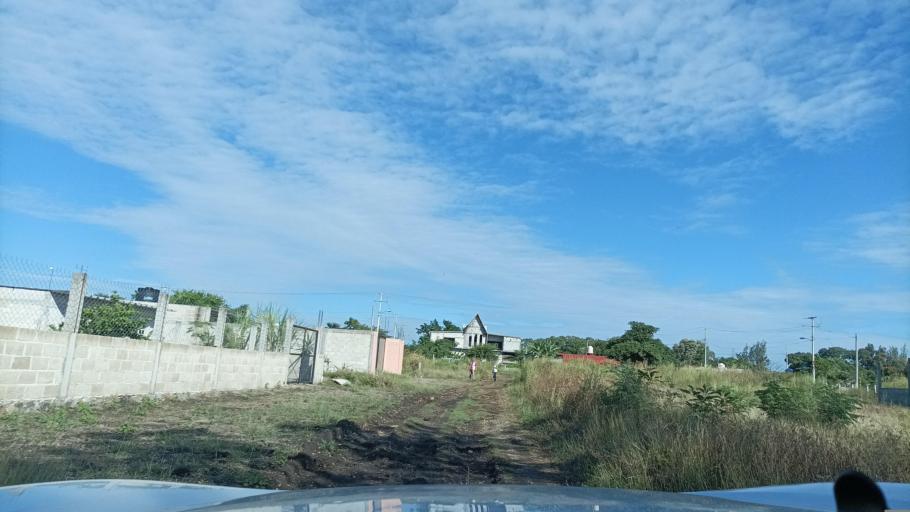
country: MX
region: Veracruz
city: Paso del Macho
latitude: 18.9715
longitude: -96.7131
